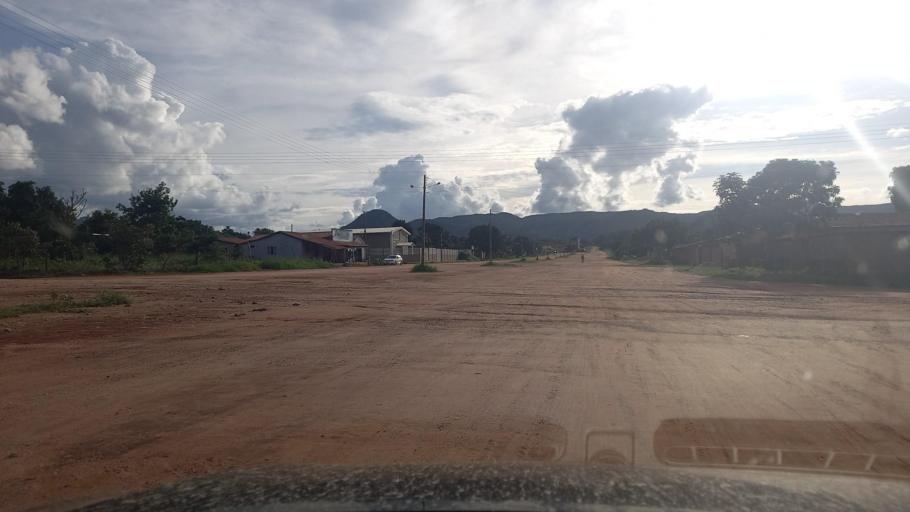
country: BR
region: Goias
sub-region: Cavalcante
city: Cavalcante
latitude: -13.7976
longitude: -47.4426
